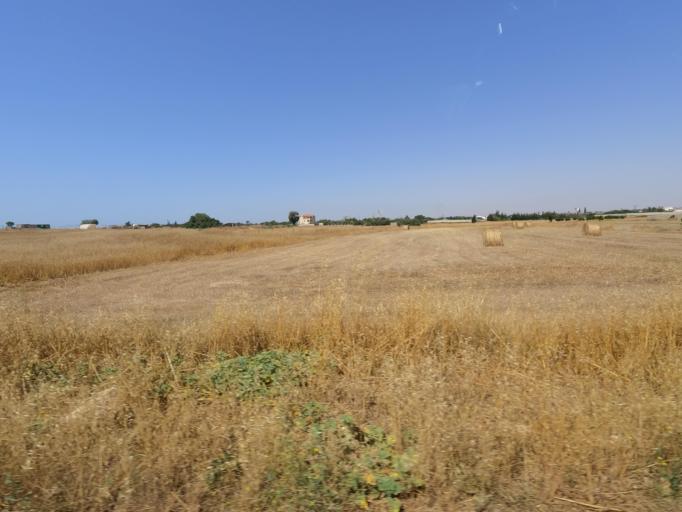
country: CY
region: Ammochostos
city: Paralimni
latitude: 35.0142
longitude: 33.9553
